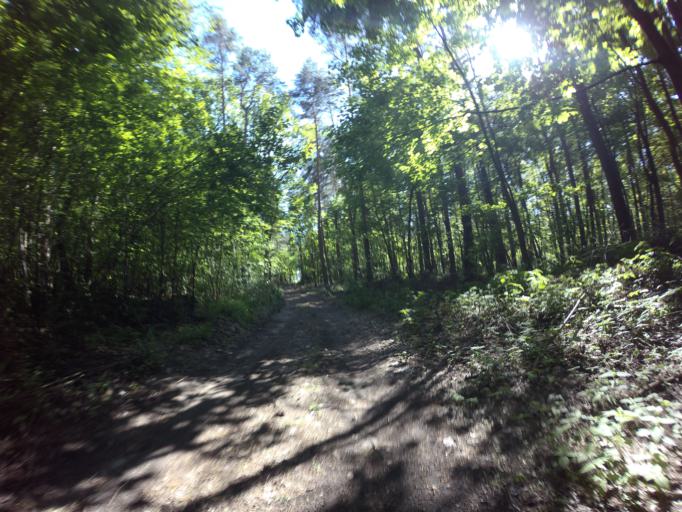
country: PL
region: West Pomeranian Voivodeship
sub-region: Powiat choszczenski
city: Choszczno
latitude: 53.1604
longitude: 15.3804
